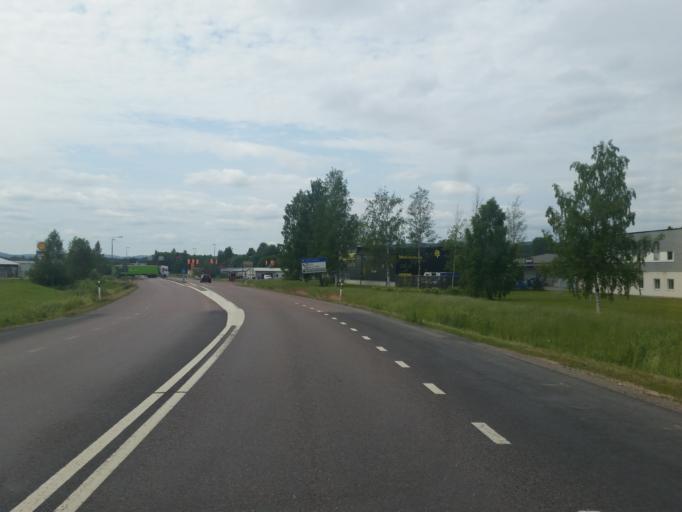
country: SE
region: Dalarna
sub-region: Borlange Kommun
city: Borlaenge
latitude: 60.4784
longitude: 15.4100
